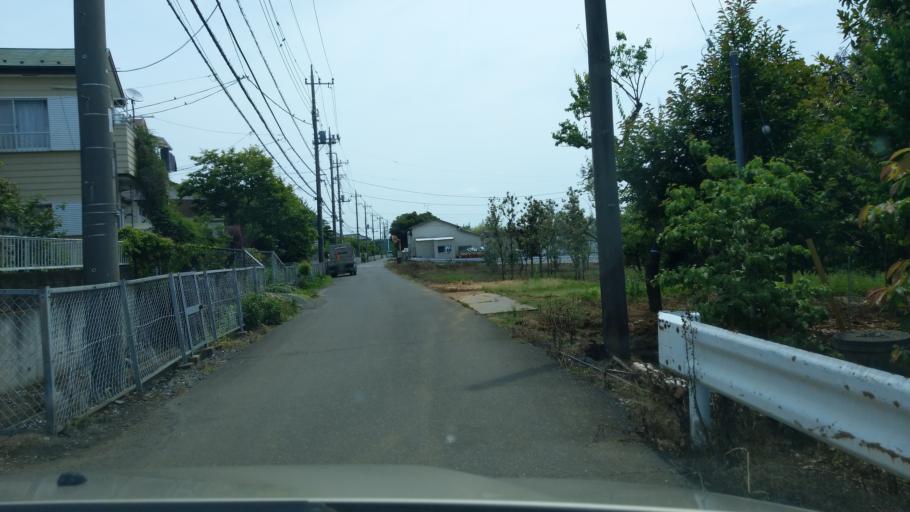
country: JP
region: Saitama
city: Saitama
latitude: 35.8971
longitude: 139.6916
